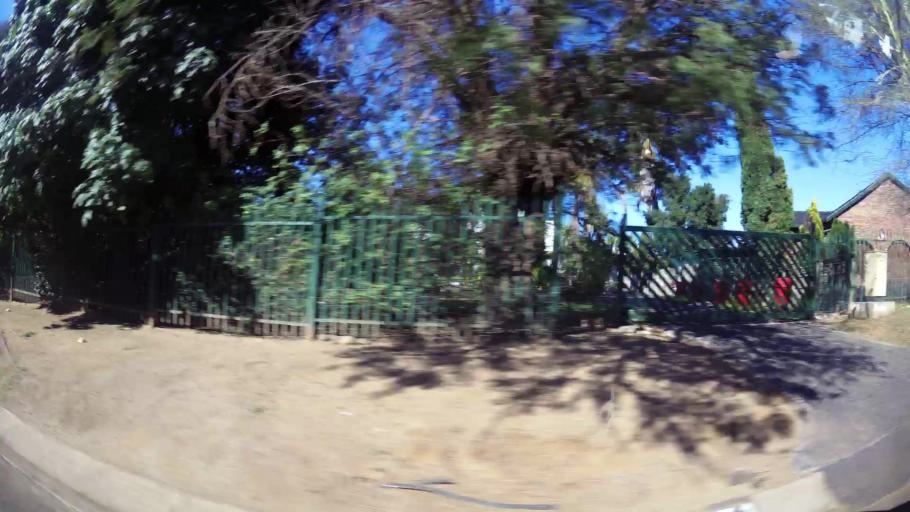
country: ZA
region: Mpumalanga
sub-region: Nkangala District Municipality
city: Witbank
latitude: -25.8720
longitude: 29.2499
